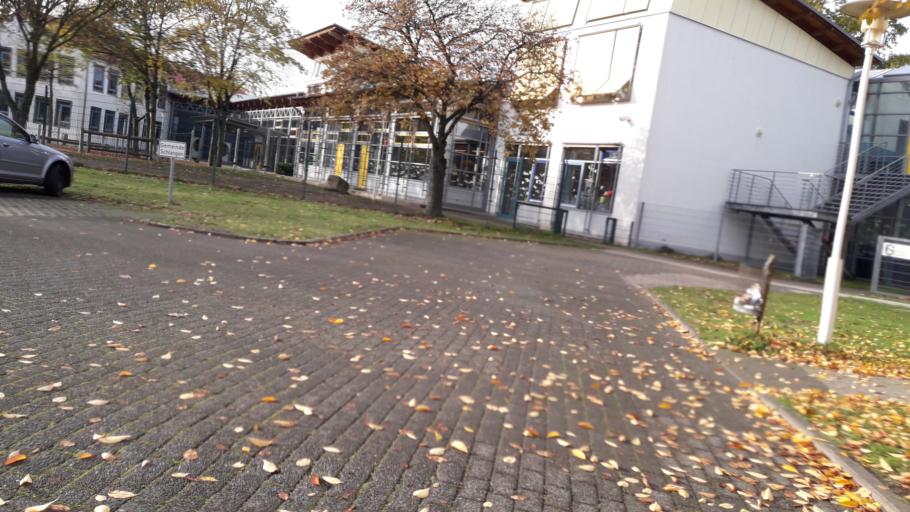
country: DE
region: North Rhine-Westphalia
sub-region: Regierungsbezirk Detmold
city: Schlangen
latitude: 51.8114
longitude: 8.8415
